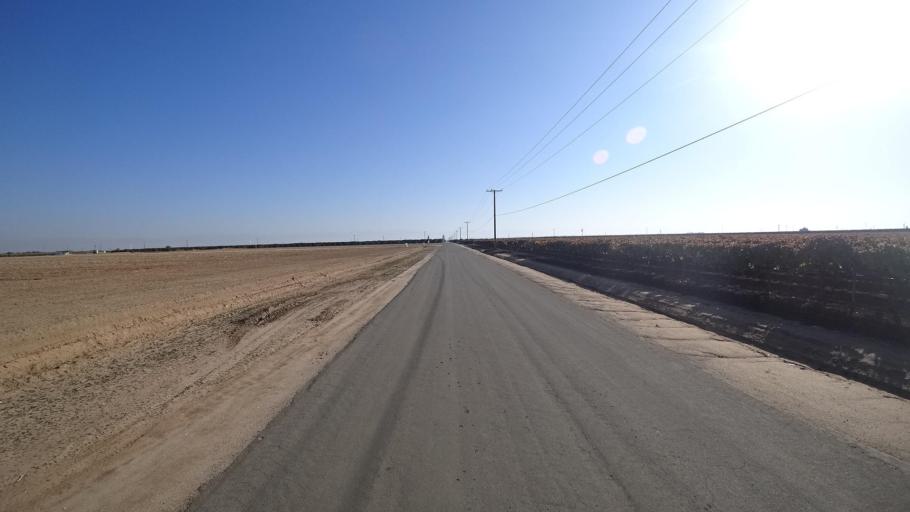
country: US
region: California
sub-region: Tulare County
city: Richgrove
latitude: 35.7328
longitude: -119.1463
